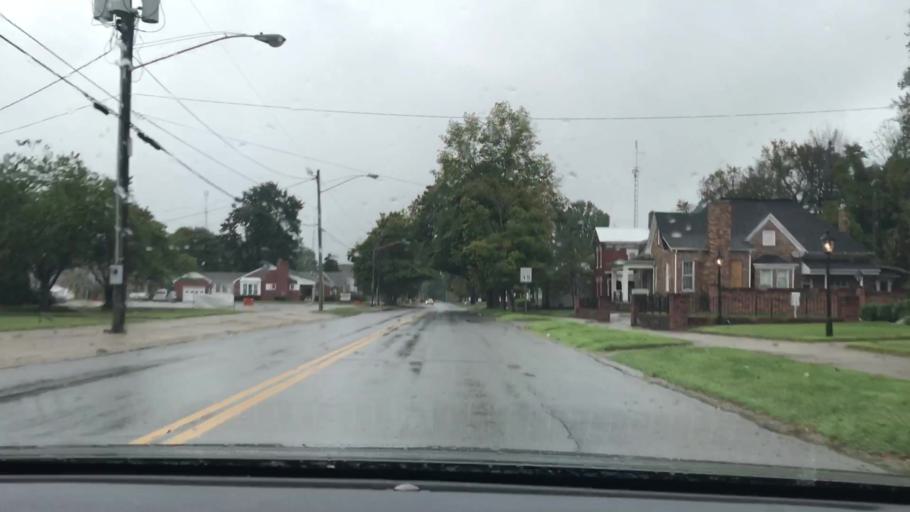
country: US
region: Kentucky
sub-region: McLean County
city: Calhoun
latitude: 37.5384
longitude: -87.2584
